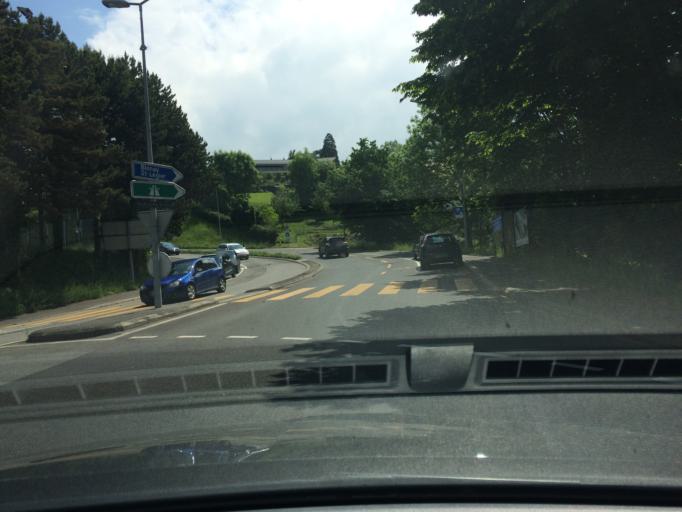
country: CH
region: Vaud
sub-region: Riviera-Pays-d'Enhaut District
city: Vevey
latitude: 46.4708
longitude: 6.8529
